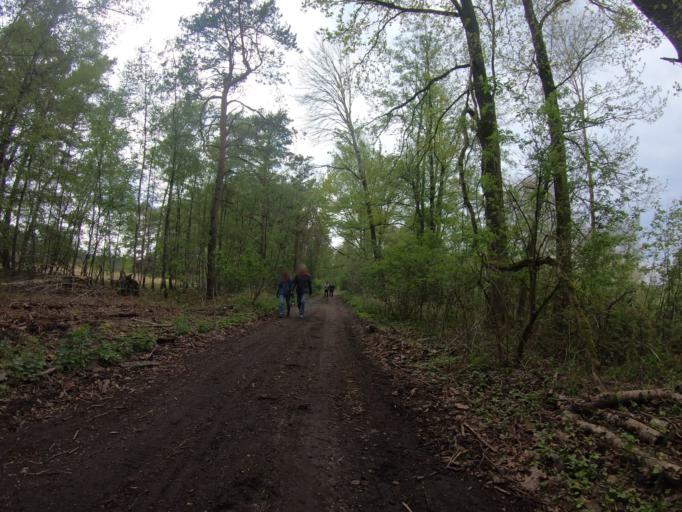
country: DE
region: Lower Saxony
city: Gifhorn
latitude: 52.4698
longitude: 10.5167
